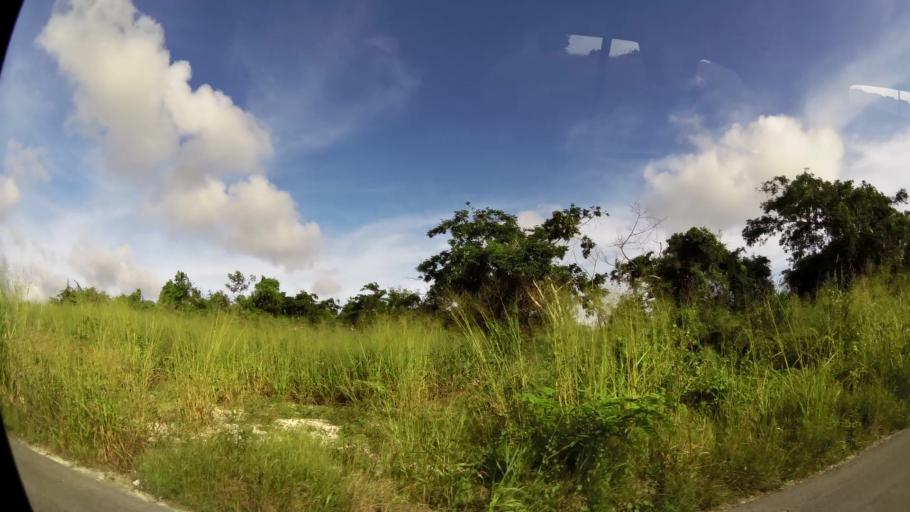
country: BB
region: Christ Church
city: Oistins
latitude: 13.0823
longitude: -59.5568
